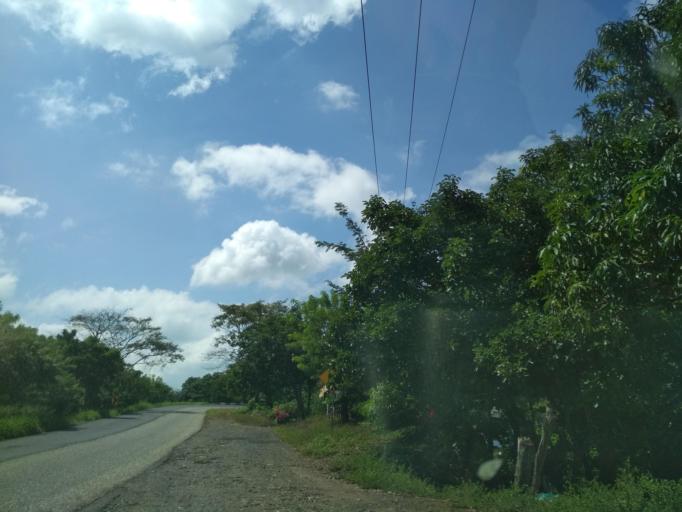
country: MX
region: Veracruz
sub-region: San Andres Tuxtla
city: Texcaltitan Xoteapan (Texcaltitan)
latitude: 18.4406
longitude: -95.2635
